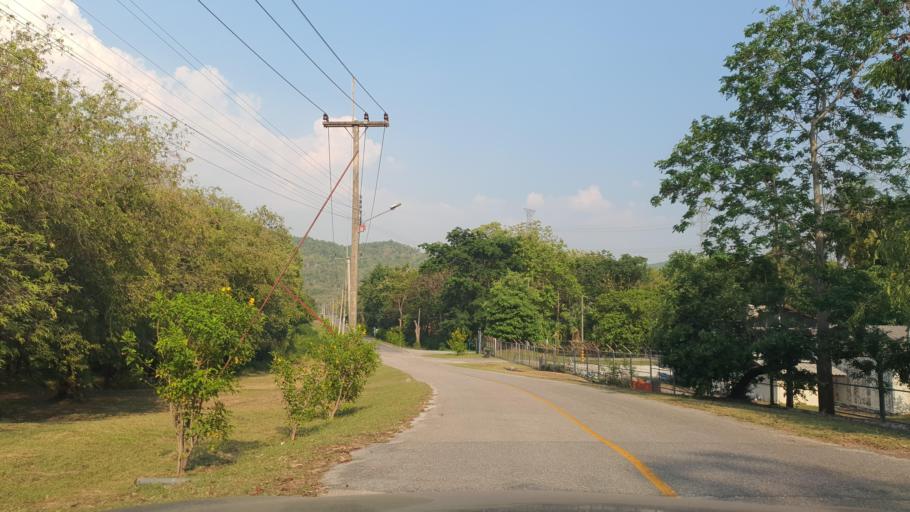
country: TH
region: Kanchanaburi
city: Sai Yok
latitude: 14.2300
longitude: 99.2301
